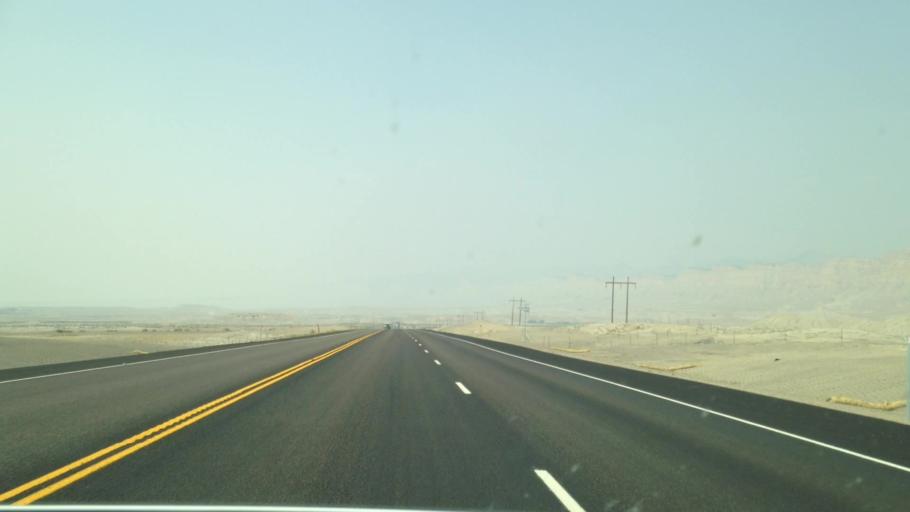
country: US
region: Utah
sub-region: Carbon County
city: East Carbon City
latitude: 39.2184
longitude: -110.3388
